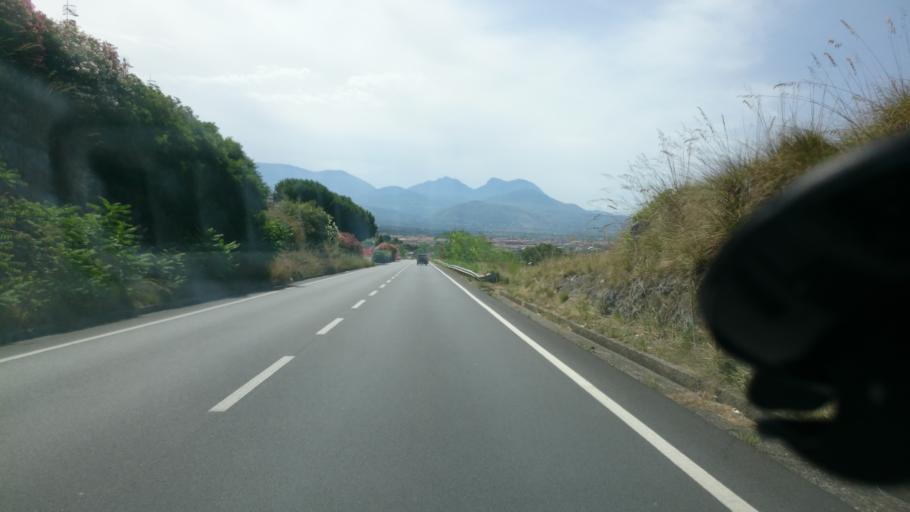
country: IT
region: Calabria
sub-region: Provincia di Cosenza
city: San Nicola Arcella
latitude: 39.8238
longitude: 15.7800
